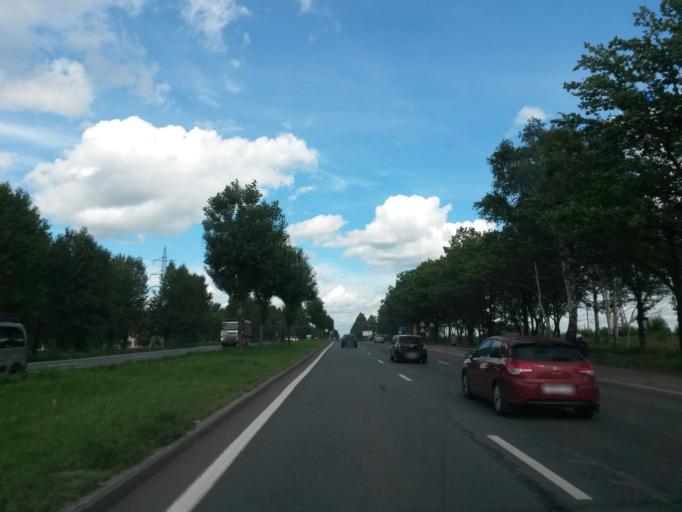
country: RU
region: Jaroslavl
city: Krasnyye Tkachi
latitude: 57.5517
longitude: 39.8112
